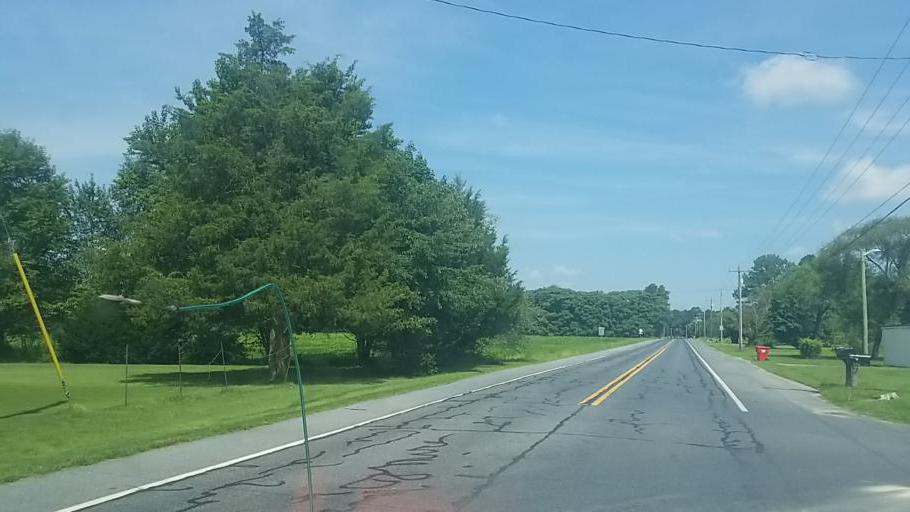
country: US
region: Delaware
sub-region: Sussex County
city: Seaford
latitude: 38.6703
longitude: -75.5726
